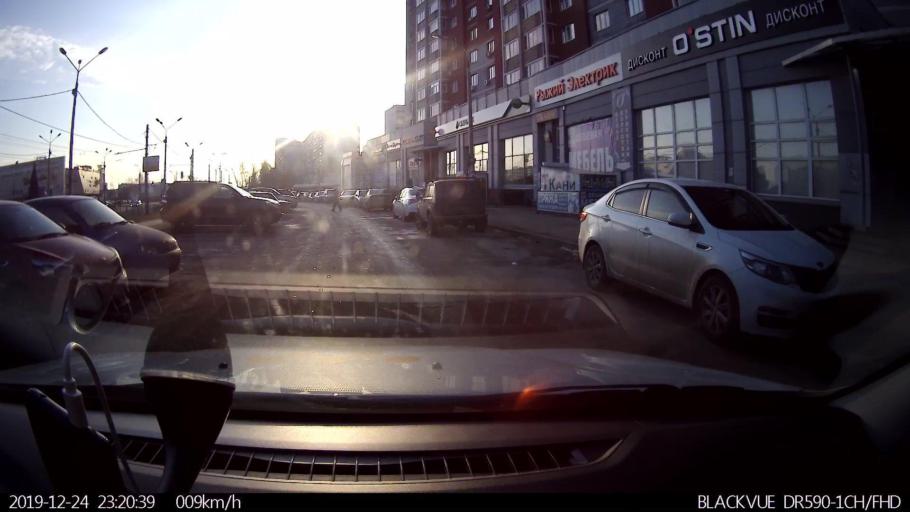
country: RU
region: Nizjnij Novgorod
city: Gorbatovka
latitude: 56.2589
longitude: 43.8536
